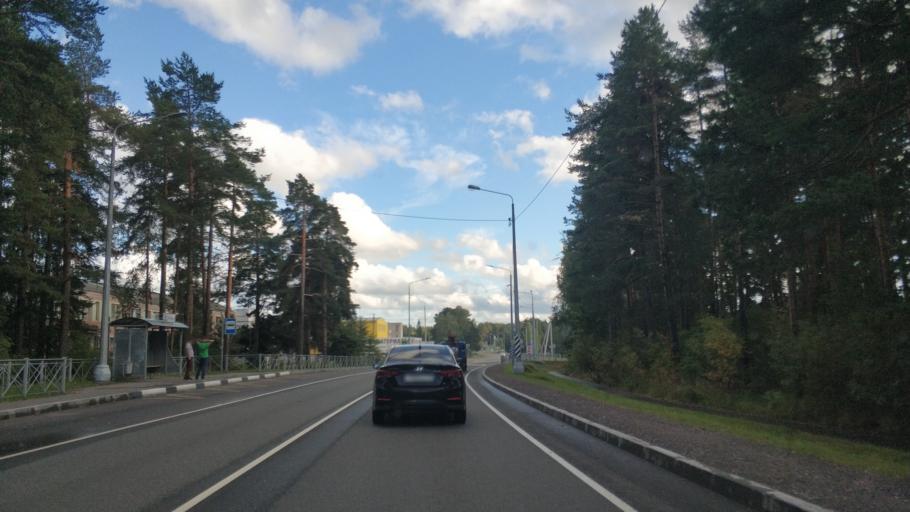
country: RU
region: Leningrad
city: Priozersk
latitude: 61.0035
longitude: 30.1806
